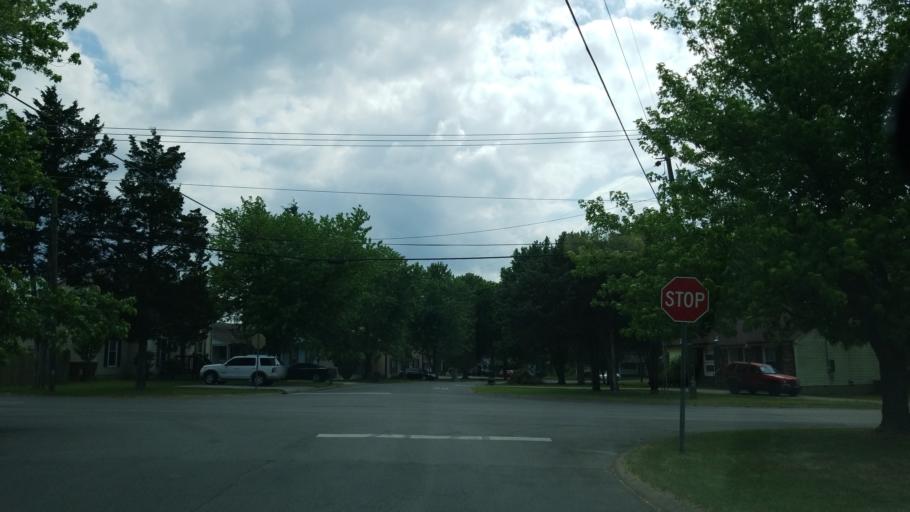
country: US
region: Tennessee
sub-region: Rutherford County
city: La Vergne
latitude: 36.0687
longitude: -86.6235
